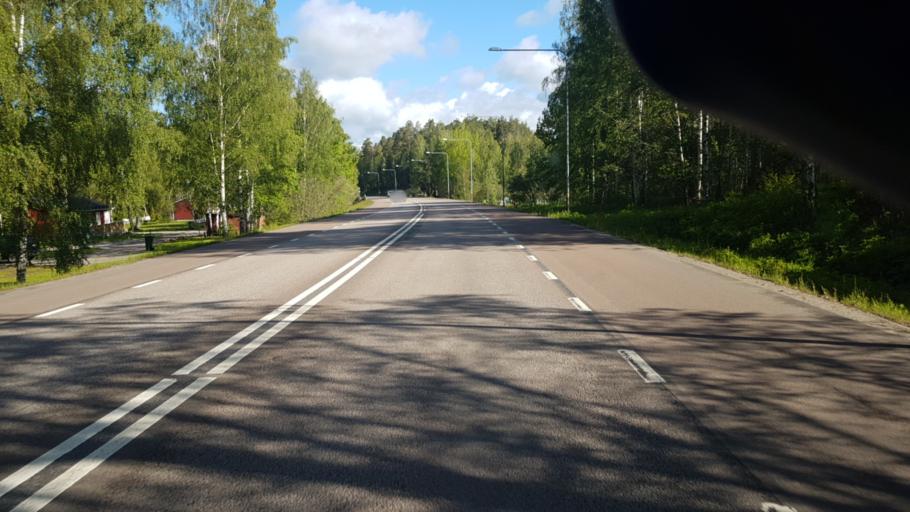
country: SE
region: Vaermland
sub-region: Arvika Kommun
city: Arvika
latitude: 59.6565
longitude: 12.6191
